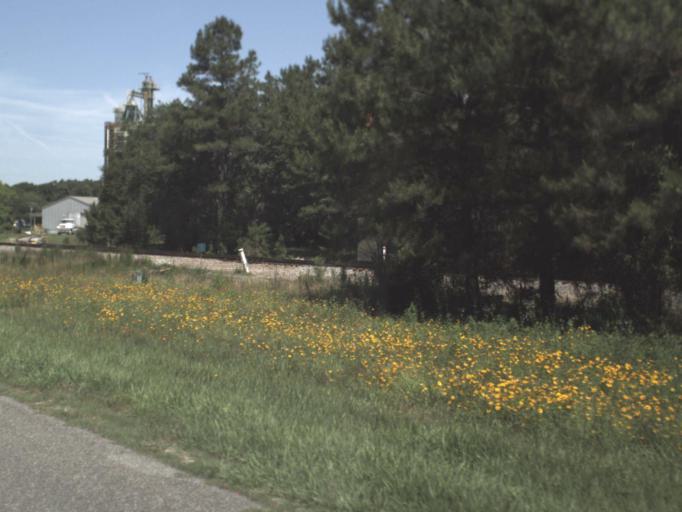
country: US
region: Florida
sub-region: Suwannee County
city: Live Oak
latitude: 30.2799
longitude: -82.9454
